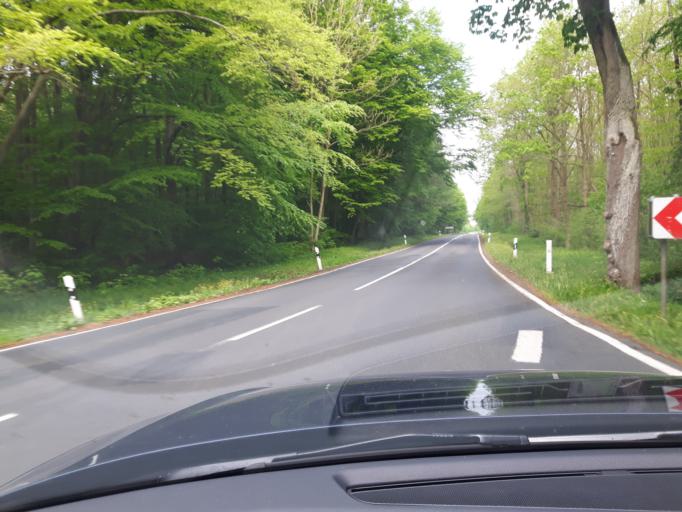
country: DE
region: Mecklenburg-Vorpommern
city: Velgast
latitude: 54.2299
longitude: 12.7301
